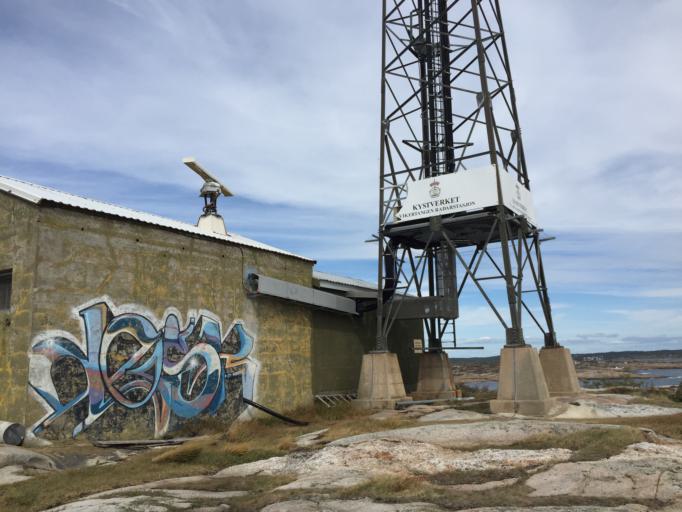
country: NO
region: Ostfold
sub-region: Hvaler
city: Skjaerhalden
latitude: 59.0334
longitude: 10.9446
